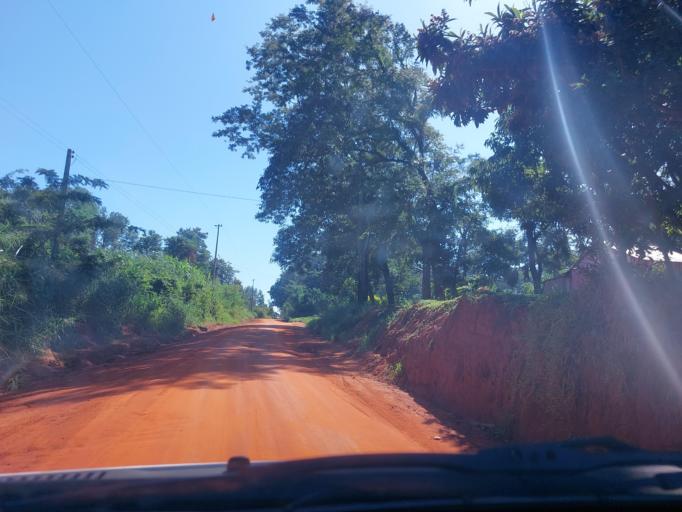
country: PY
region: San Pedro
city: Lima
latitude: -24.1664
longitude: -56.0134
